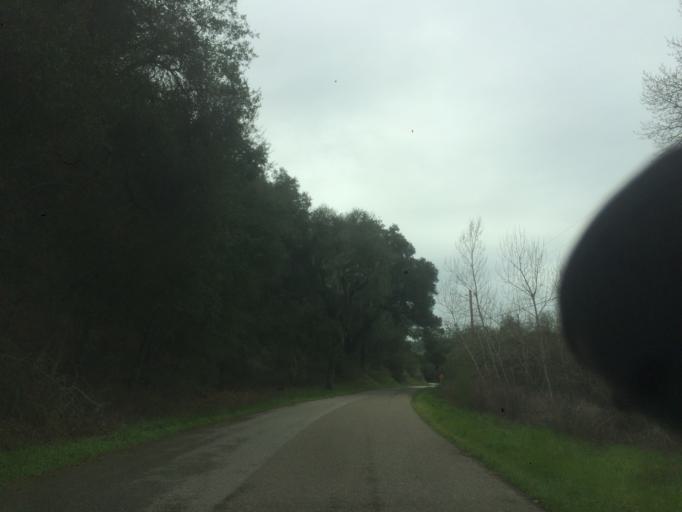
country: US
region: California
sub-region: San Luis Obispo County
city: Nipomo
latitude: 35.2070
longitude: -120.4108
